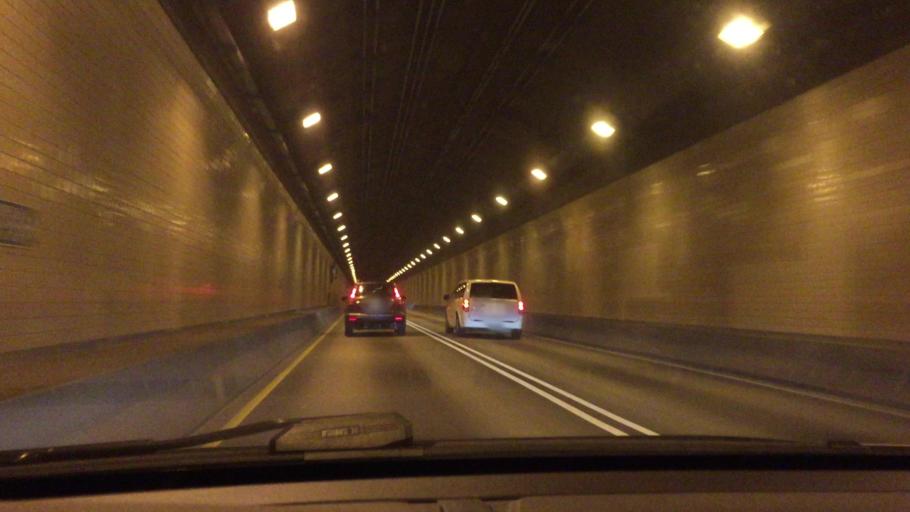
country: US
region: Pennsylvania
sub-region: Allegheny County
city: Homestead
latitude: 40.4272
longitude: -79.9202
